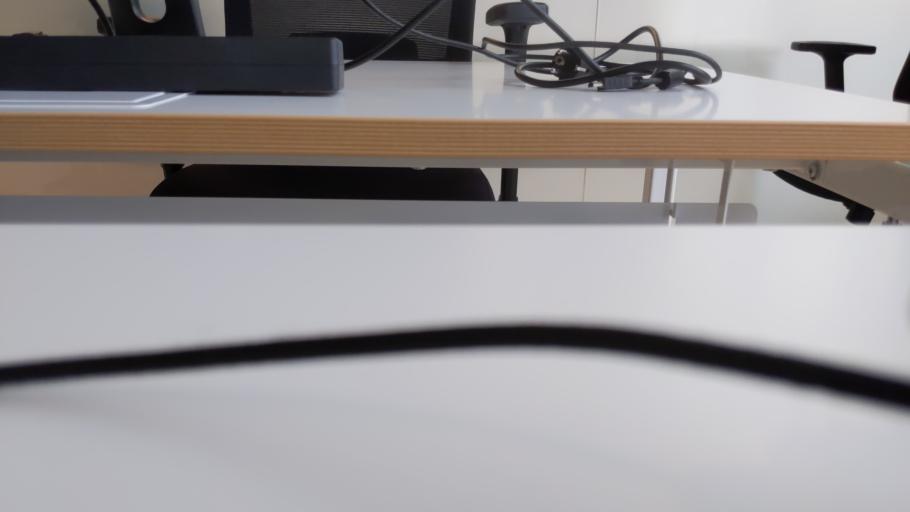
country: RU
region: Moskovskaya
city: Shevlyakovo
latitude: 56.4213
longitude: 36.9751
